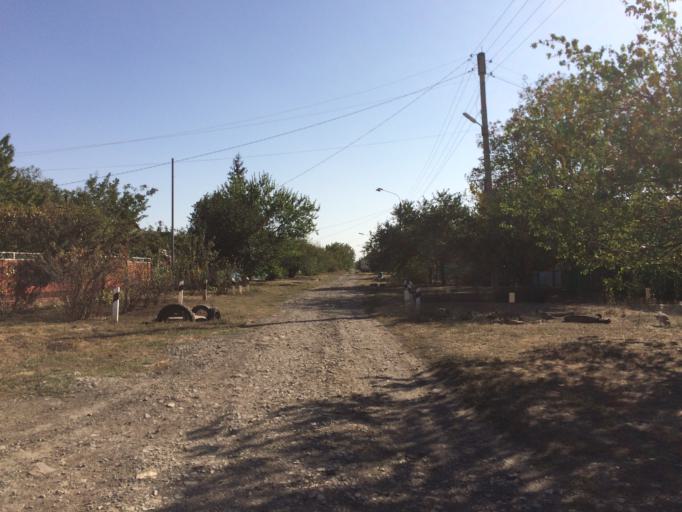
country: RU
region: Rostov
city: Tselina
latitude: 46.5272
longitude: 41.1860
